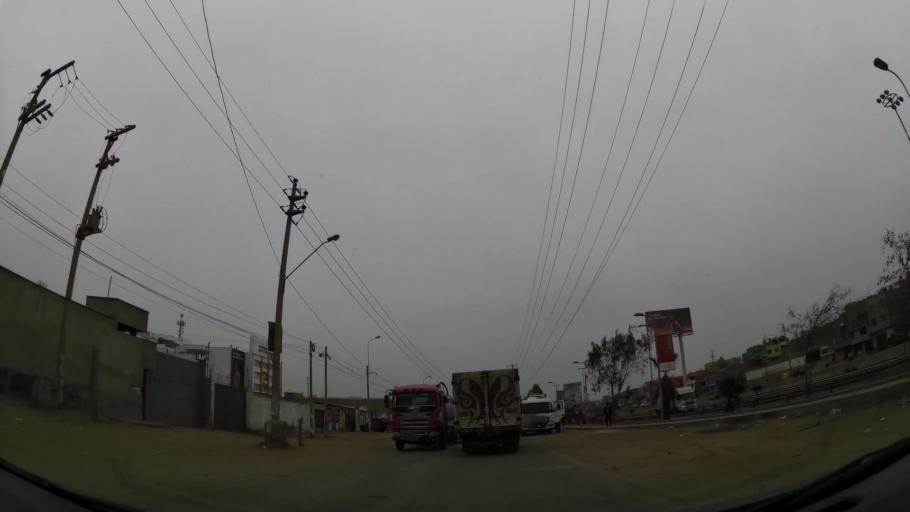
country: PE
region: Lima
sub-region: Lima
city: Surco
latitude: -12.1943
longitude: -76.9724
